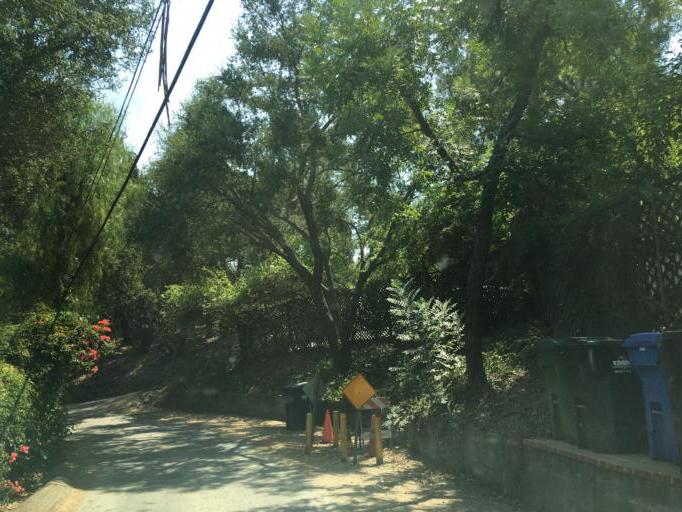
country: US
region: California
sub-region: Los Angeles County
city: Topanga
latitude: 34.0899
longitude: -118.5911
